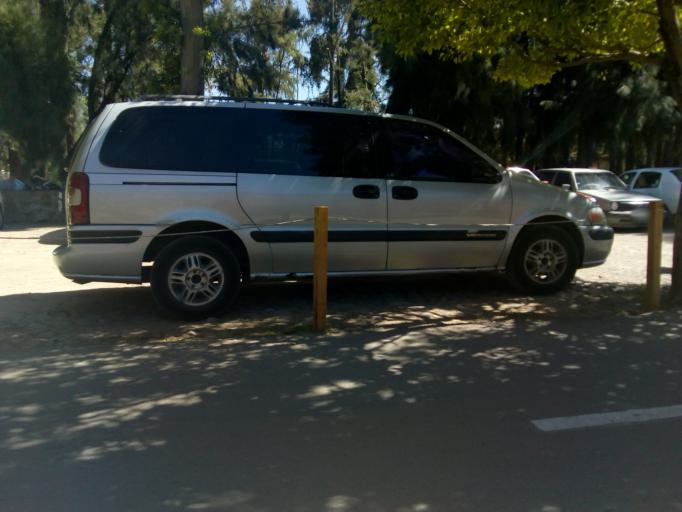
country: MX
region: Guanajuato
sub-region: Leon
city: La Ermita
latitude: 21.1729
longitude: -101.6916
